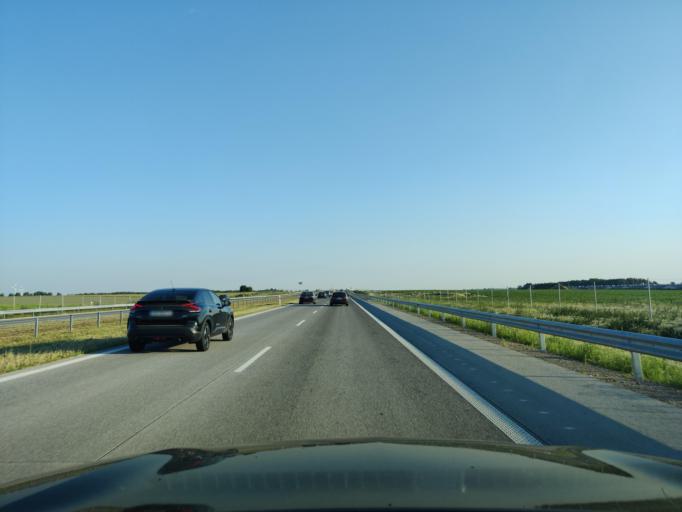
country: PL
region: Masovian Voivodeship
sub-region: Powiat mlawski
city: Wisniewo
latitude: 53.0551
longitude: 20.3630
